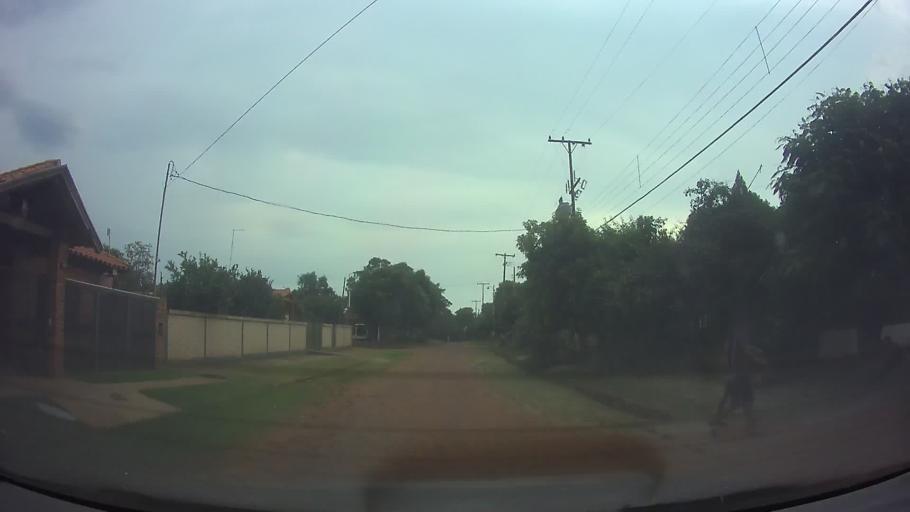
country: PY
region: Central
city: San Lorenzo
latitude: -25.2603
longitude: -57.4630
